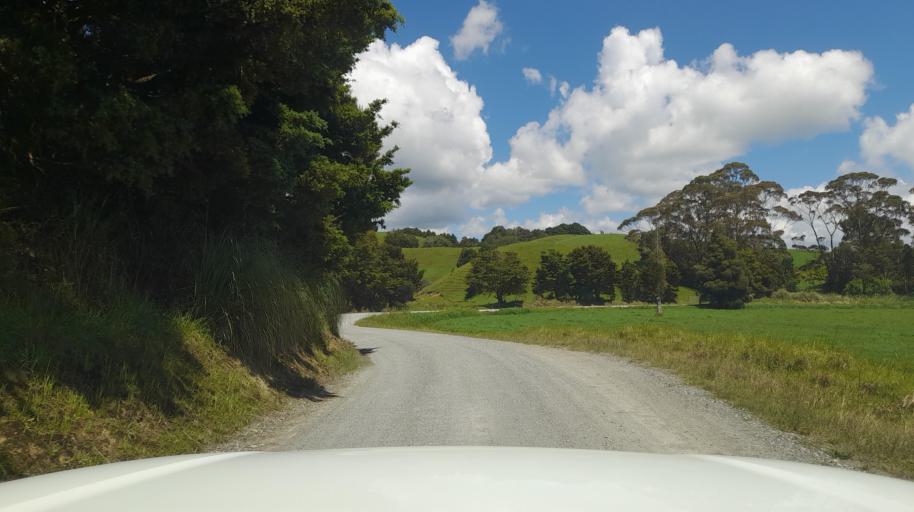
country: NZ
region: Northland
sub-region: Far North District
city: Kaitaia
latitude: -35.1121
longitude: 173.3965
